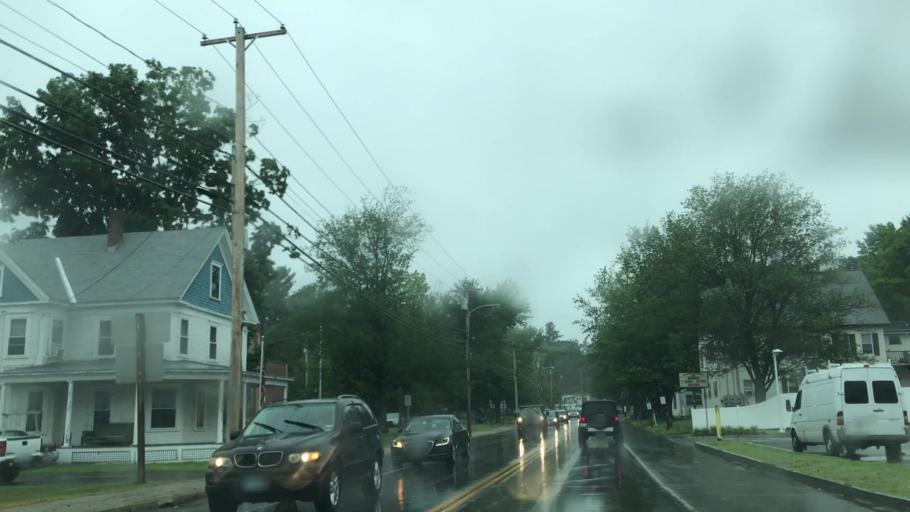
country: US
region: Maine
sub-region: York County
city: Berwick
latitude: 43.2680
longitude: -70.8616
